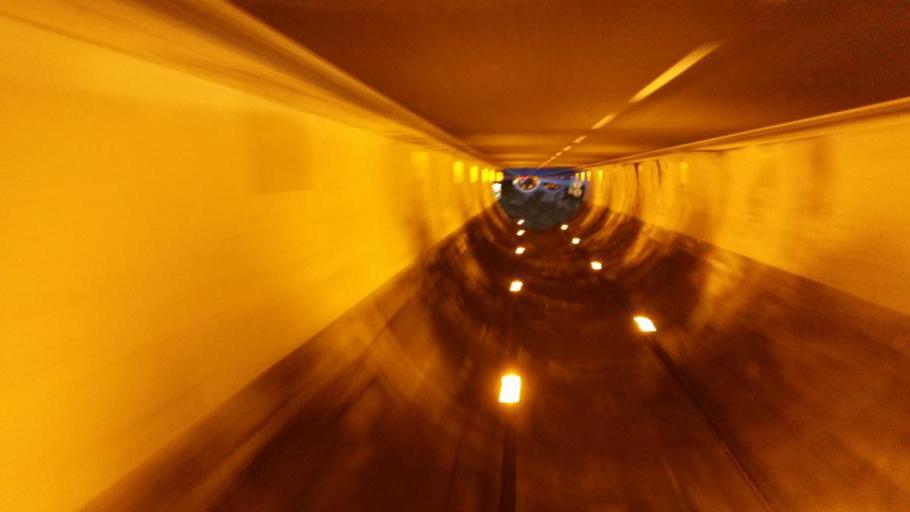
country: IT
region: Liguria
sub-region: Provincia di Imperia
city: Terzorio
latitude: 43.8510
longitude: 7.9121
